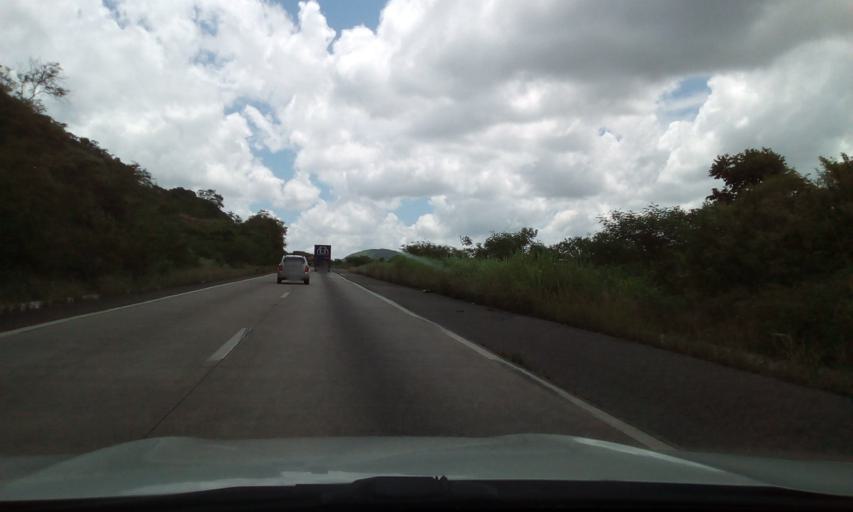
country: BR
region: Pernambuco
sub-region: Pombos
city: Pombos
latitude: -8.1611
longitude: -35.4374
